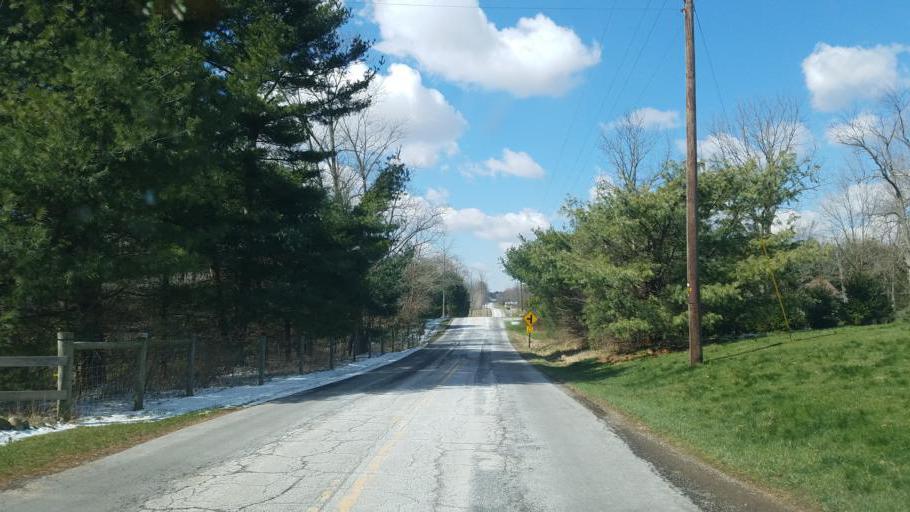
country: US
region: Ohio
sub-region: Knox County
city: Mount Vernon
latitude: 40.3141
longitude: -82.5488
